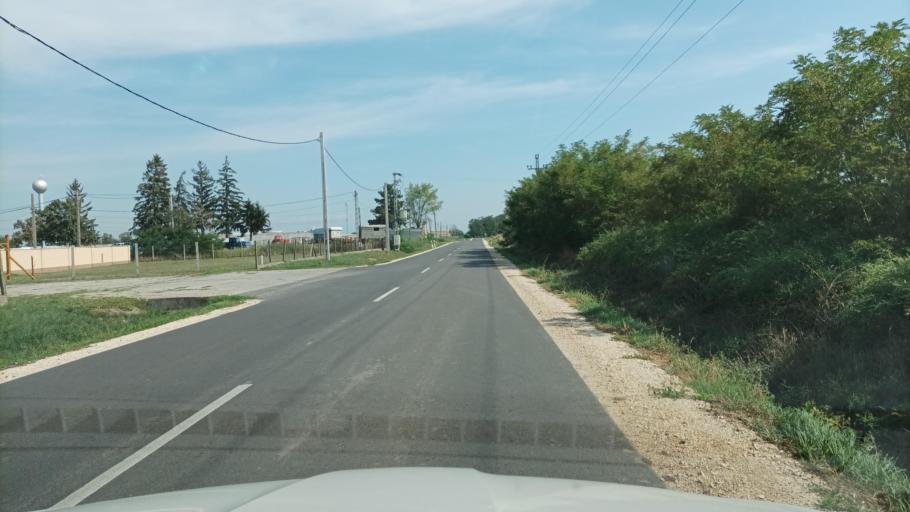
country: HU
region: Pest
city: Galgaheviz
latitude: 47.5926
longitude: 19.5751
